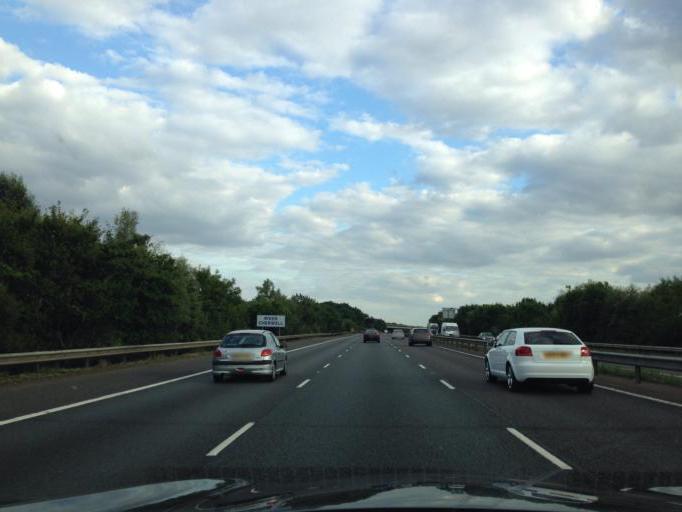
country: GB
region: England
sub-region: Oxfordshire
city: Adderbury
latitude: 52.0129
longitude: -1.2803
